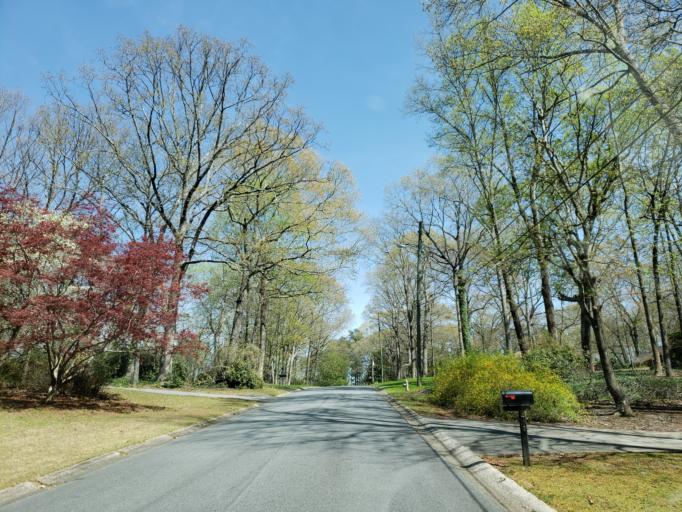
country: US
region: Georgia
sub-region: Cobb County
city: Marietta
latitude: 33.9639
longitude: -84.5701
